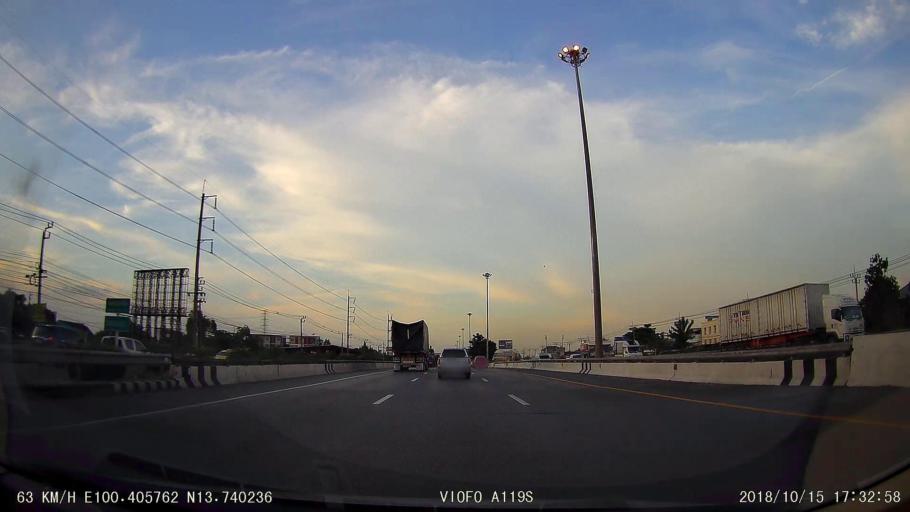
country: TH
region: Bangkok
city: Phasi Charoen
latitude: 13.7402
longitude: 100.4058
